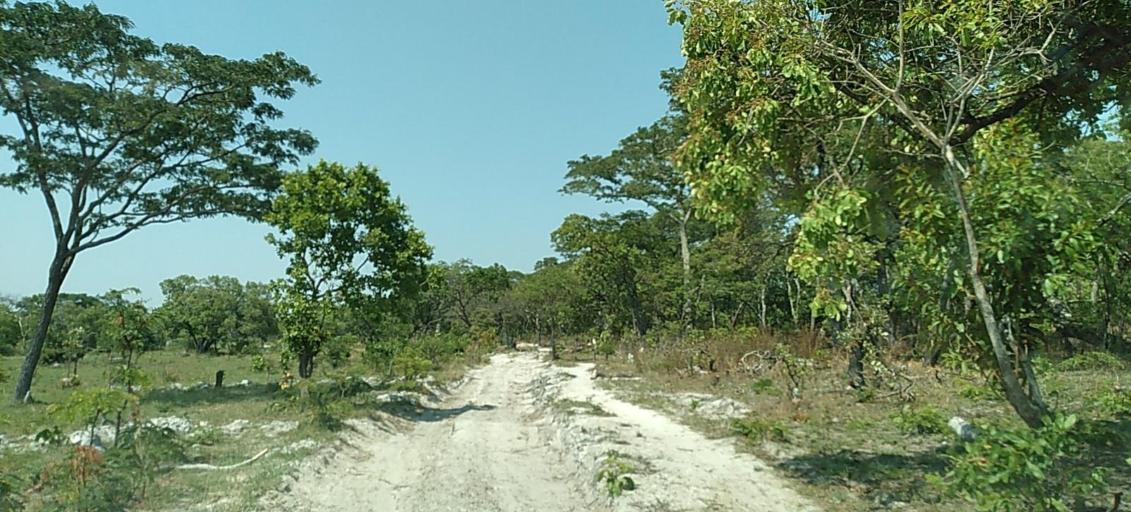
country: ZM
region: Copperbelt
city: Mpongwe
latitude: -13.7805
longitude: 28.1062
